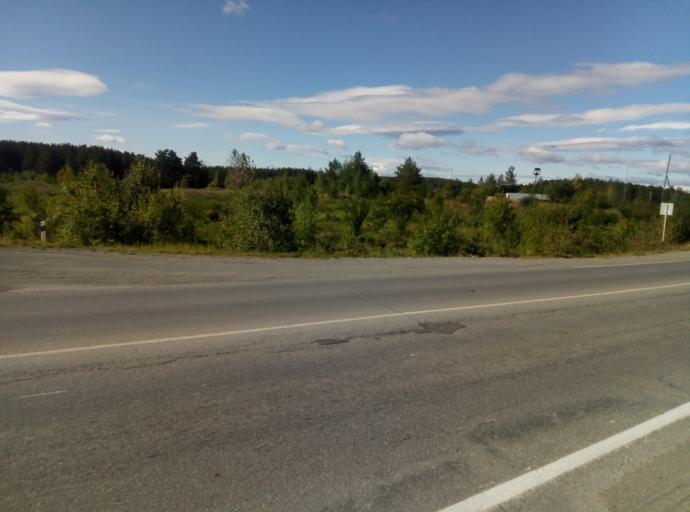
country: RU
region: Sverdlovsk
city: Karpinsk
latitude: 59.7576
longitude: 60.0485
